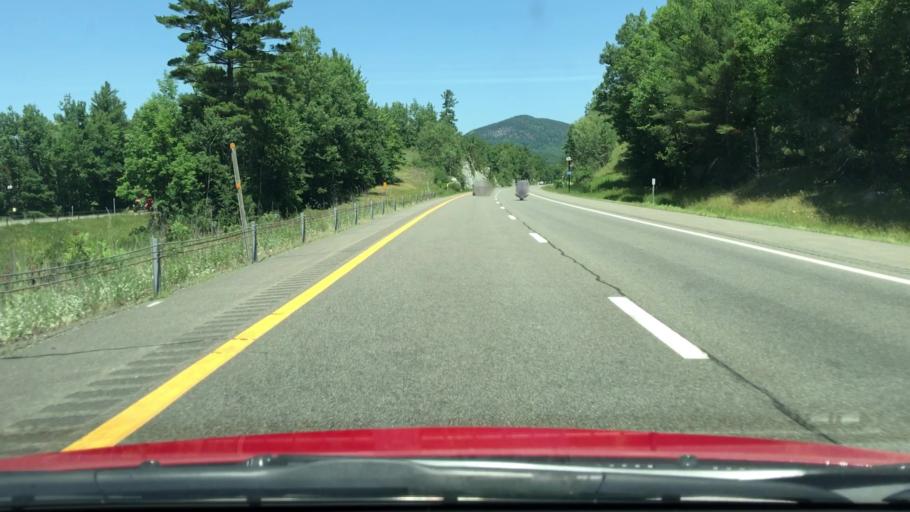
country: US
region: New York
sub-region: Essex County
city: Elizabethtown
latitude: 44.3475
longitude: -73.5331
